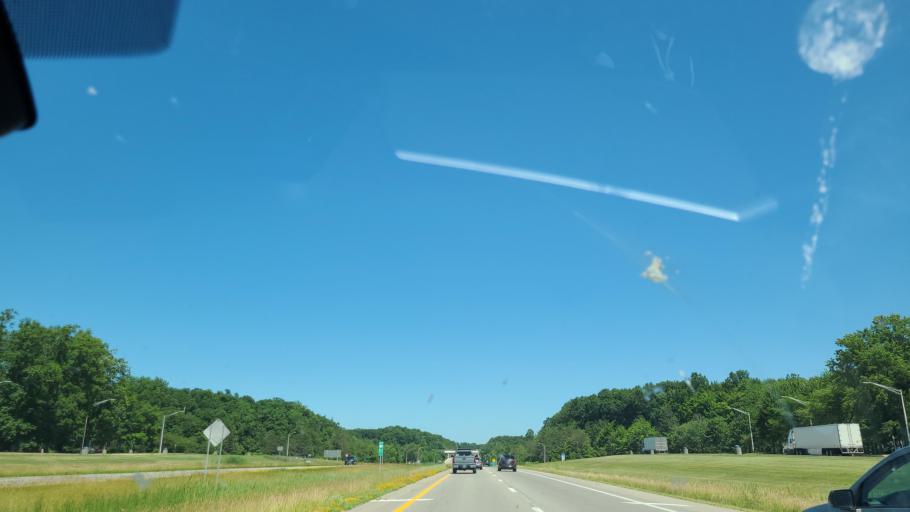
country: US
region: Ohio
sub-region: Lorain County
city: Vermilion-on-the-Lake
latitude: 41.4027
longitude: -82.3379
